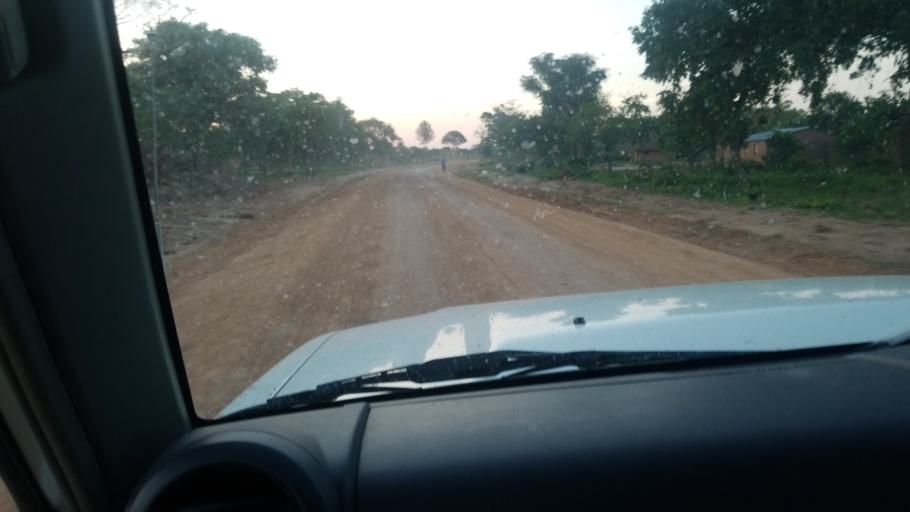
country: ZM
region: Northern
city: Luwingu
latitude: -10.5601
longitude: 29.9959
